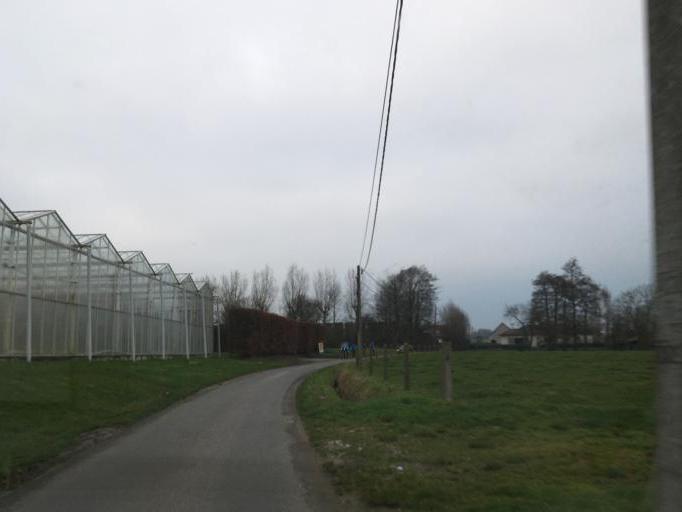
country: BE
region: Flanders
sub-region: Provincie West-Vlaanderen
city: Hooglede
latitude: 50.9801
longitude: 3.1126
